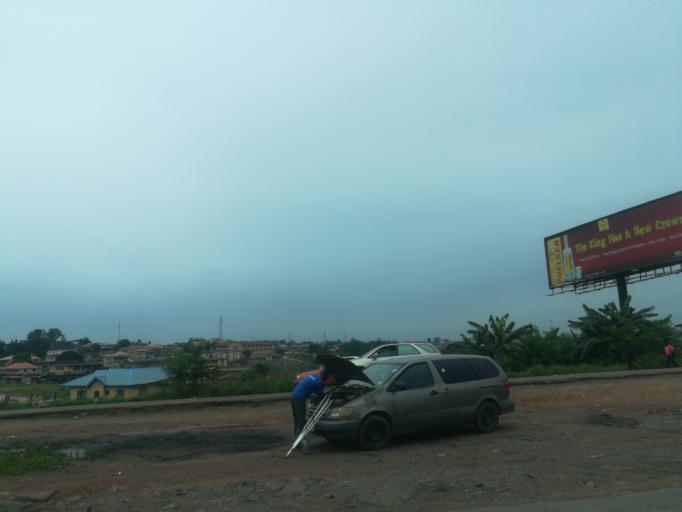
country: NG
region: Oyo
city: Ibadan
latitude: 7.3915
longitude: 3.9375
